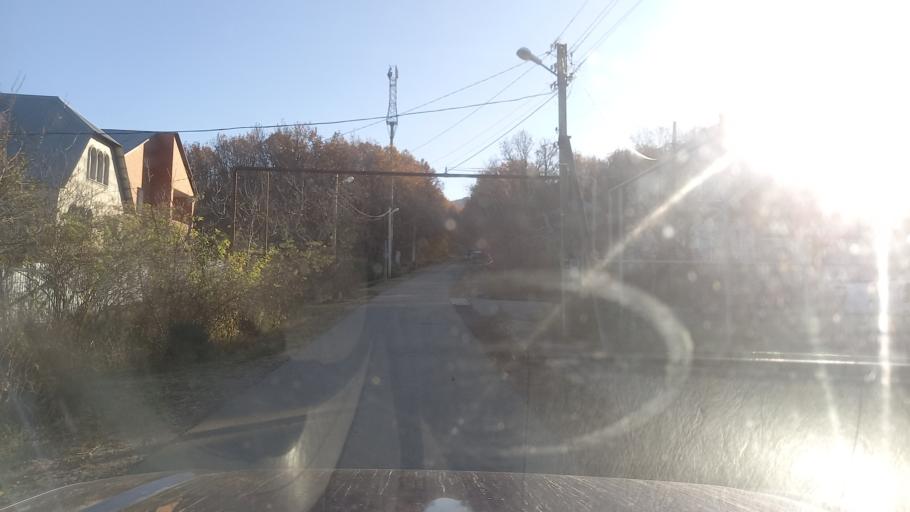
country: RU
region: Krasnodarskiy
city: Goryachiy Klyuch
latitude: 44.6188
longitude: 39.1044
